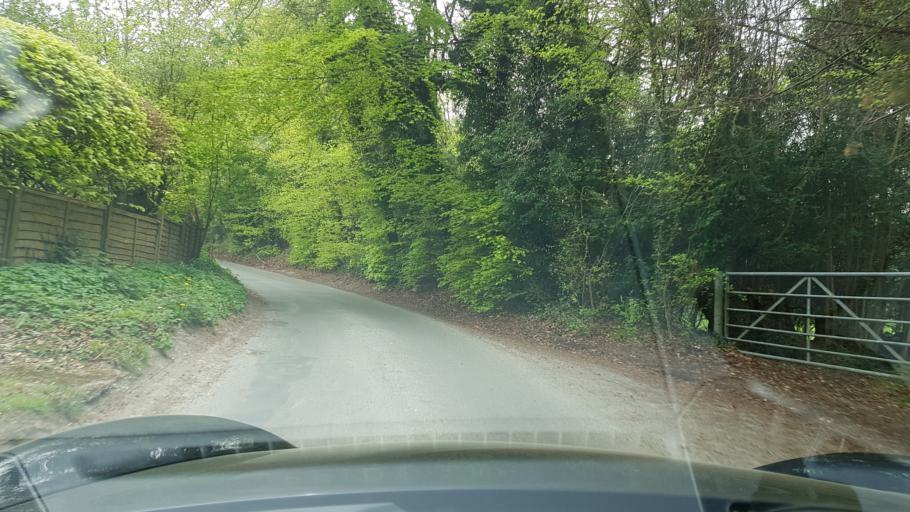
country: GB
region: England
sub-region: Surrey
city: East Horsley
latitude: 51.2512
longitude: -0.4472
